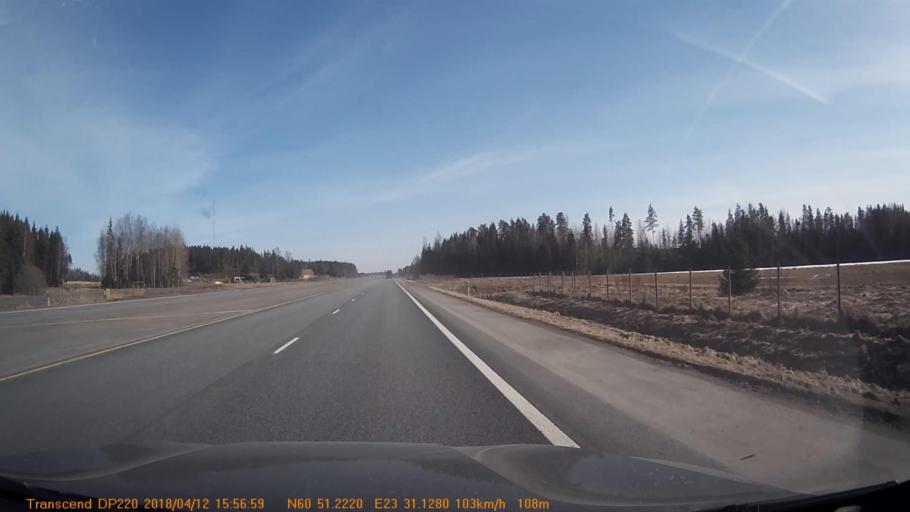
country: FI
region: Haeme
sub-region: Forssa
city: Jokioinen
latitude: 60.8536
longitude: 23.5189
